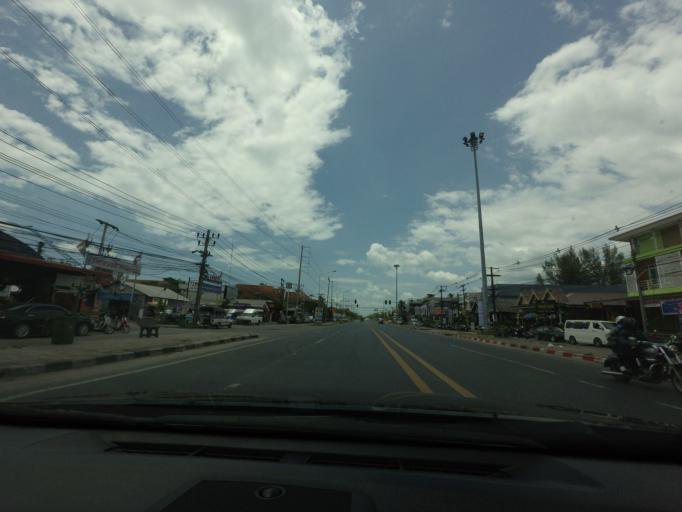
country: TH
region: Phangnga
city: Ban Khao Lak
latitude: 8.6668
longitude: 98.2531
